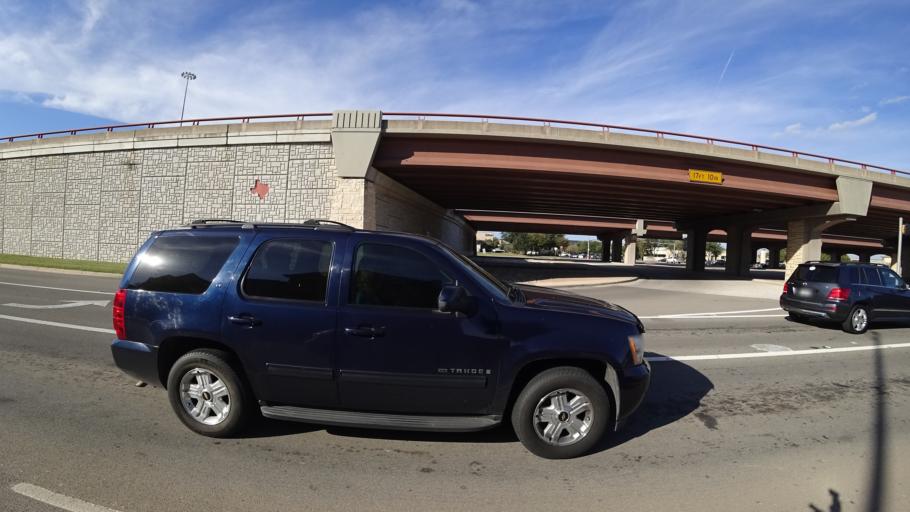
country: US
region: Texas
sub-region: Williamson County
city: Round Rock
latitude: 30.4786
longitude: -97.6860
